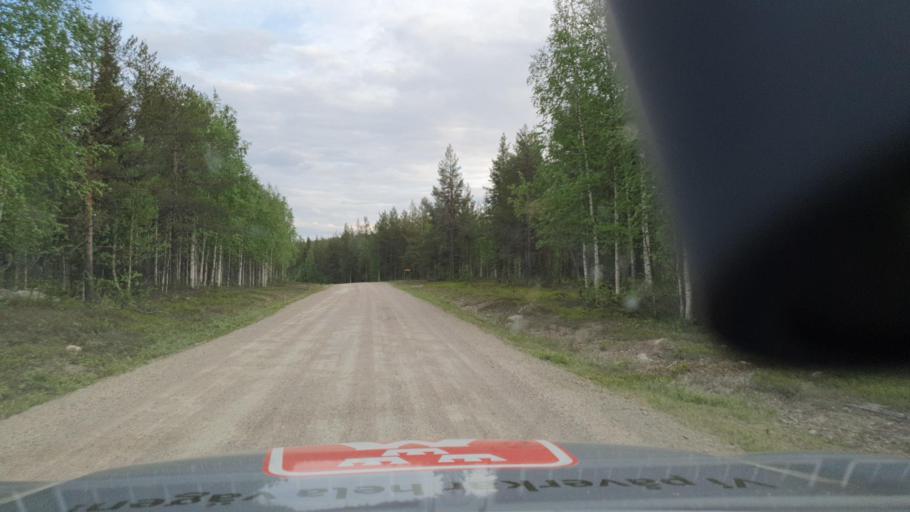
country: SE
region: Norrbotten
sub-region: Gallivare Kommun
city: Gaellivare
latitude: 66.7344
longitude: 21.1405
